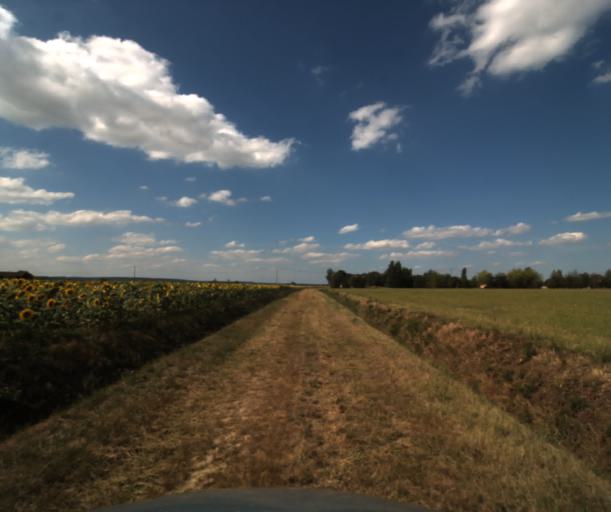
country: FR
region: Midi-Pyrenees
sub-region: Departement de la Haute-Garonne
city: Saint-Lys
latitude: 43.5273
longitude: 1.1789
